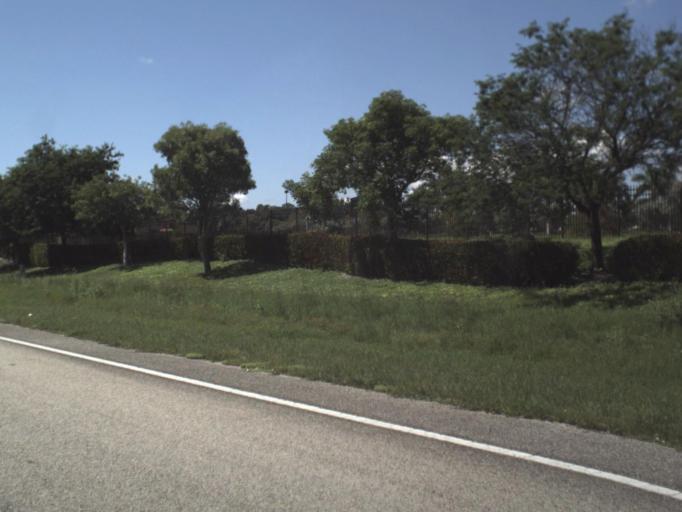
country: US
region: Florida
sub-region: Lee County
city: Lochmoor Waterway Estates
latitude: 26.6480
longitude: -81.9844
